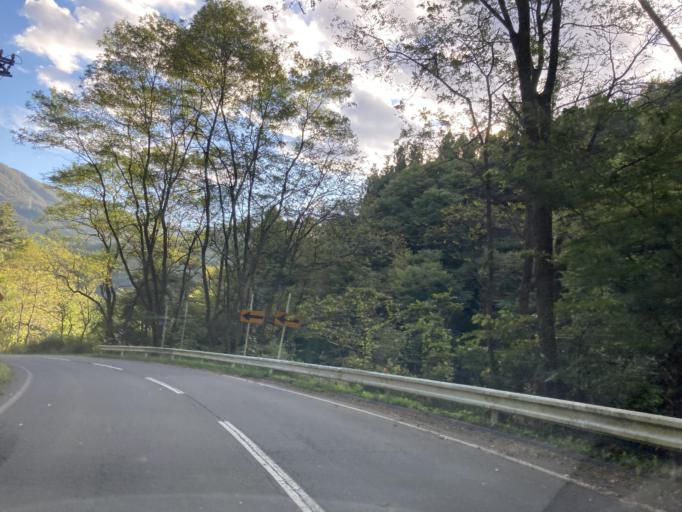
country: JP
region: Nagano
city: Ueda
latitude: 36.3955
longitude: 138.0984
